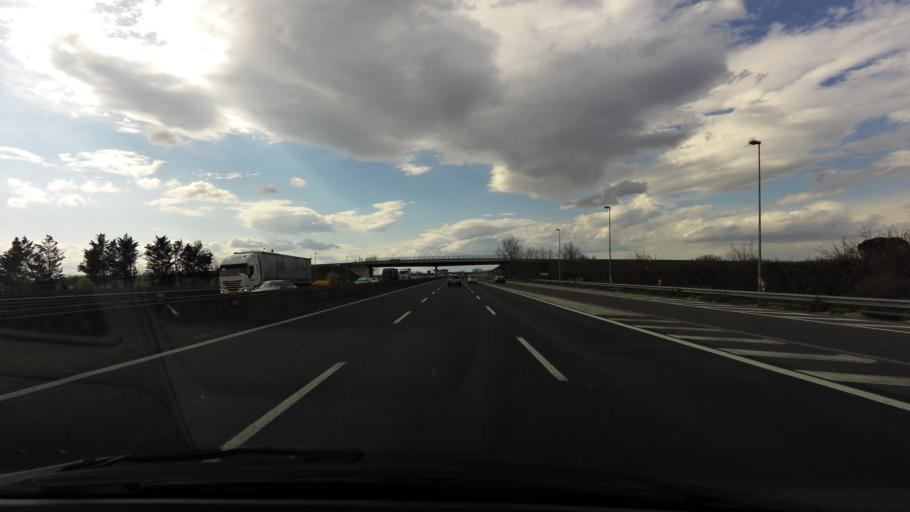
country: IT
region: Emilia-Romagna
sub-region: Provincia di Ravenna
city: Solarolo
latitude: 44.3550
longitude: 11.8123
